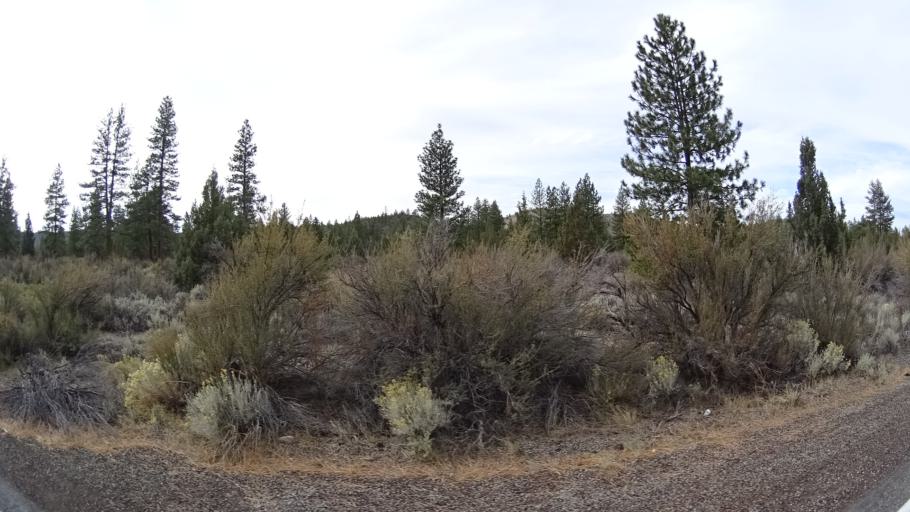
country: US
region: California
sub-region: Siskiyou County
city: Weed
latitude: 41.5398
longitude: -122.2449
